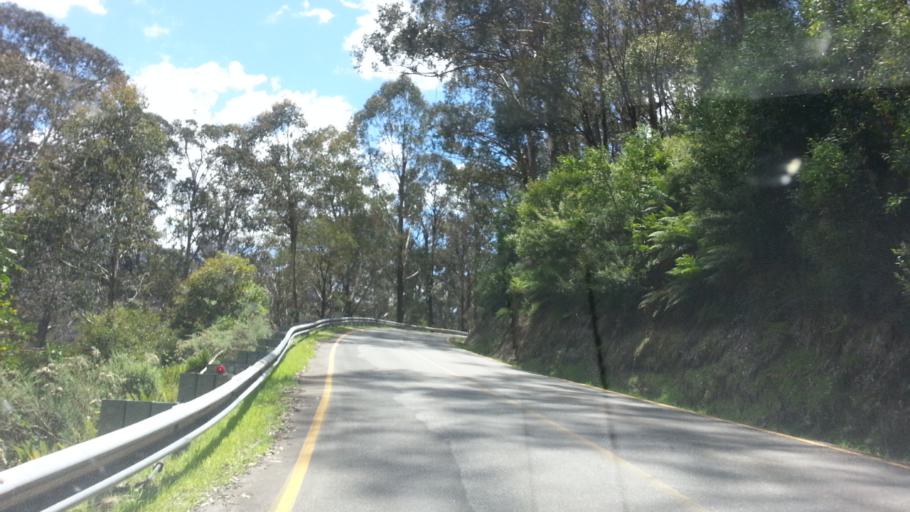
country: AU
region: Victoria
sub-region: Alpine
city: Mount Beauty
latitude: -36.8480
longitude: 147.2437
